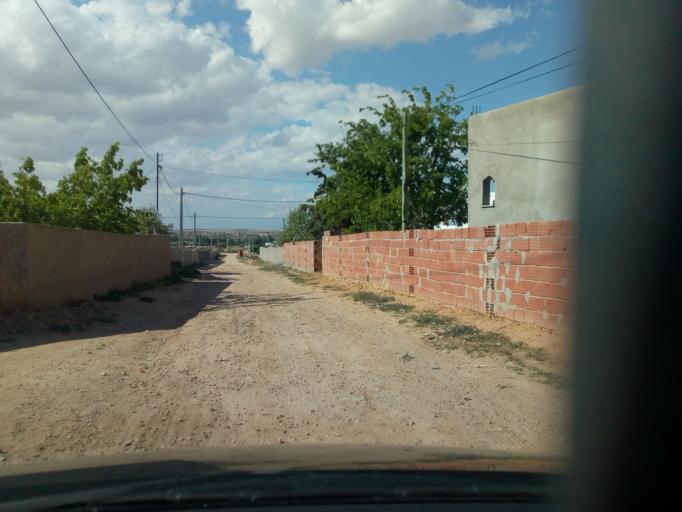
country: TN
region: Safaqis
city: Sfax
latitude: 34.7287
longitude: 10.6009
